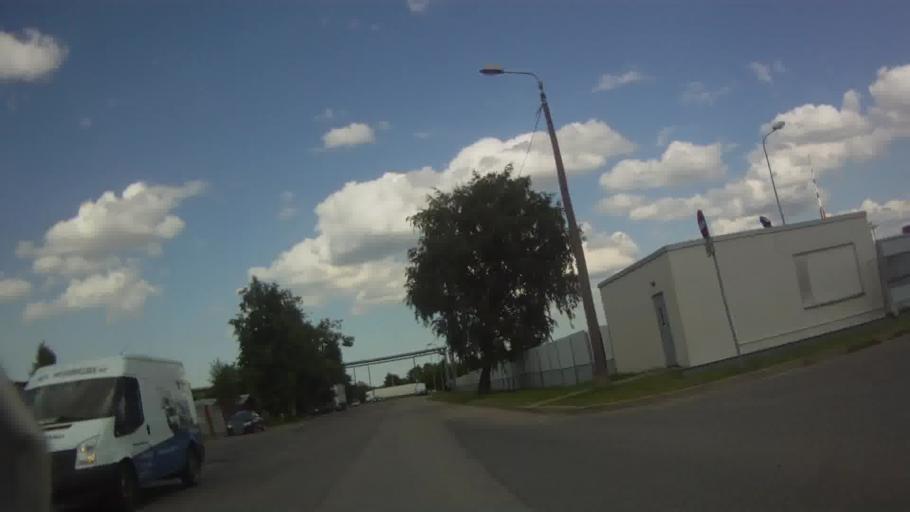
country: LV
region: Riga
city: Riga
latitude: 56.9190
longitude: 24.1085
